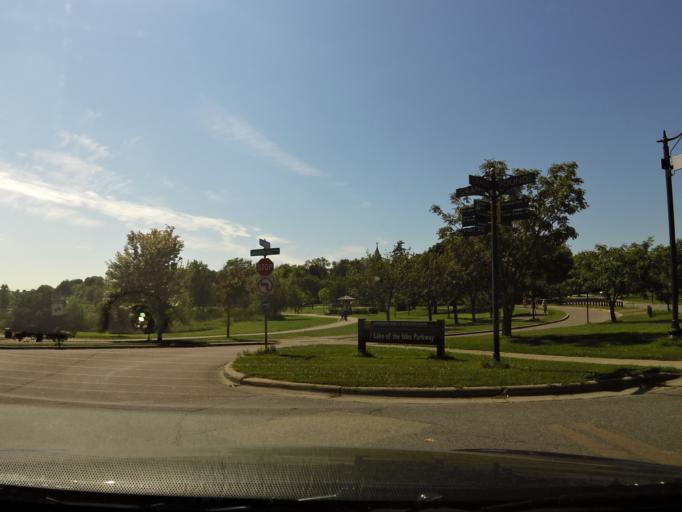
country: US
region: Minnesota
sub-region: Hennepin County
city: Minneapolis
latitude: 44.9633
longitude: -93.3037
